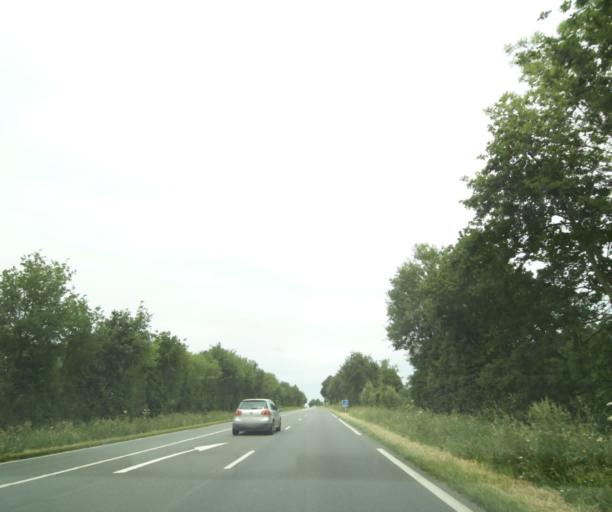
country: FR
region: Poitou-Charentes
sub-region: Departement des Deux-Sevres
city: Champdeniers-Saint-Denis
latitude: 46.4914
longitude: -0.3485
